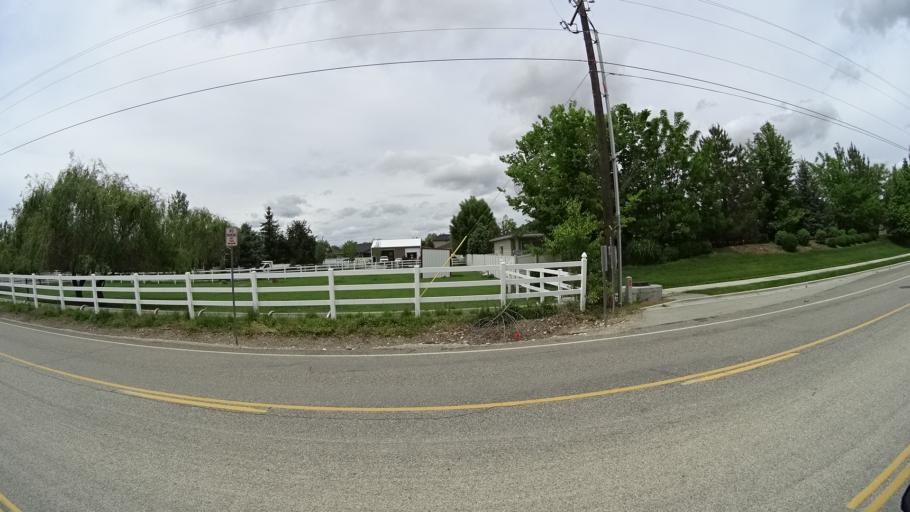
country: US
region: Idaho
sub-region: Ada County
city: Eagle
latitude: 43.7008
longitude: -116.4036
